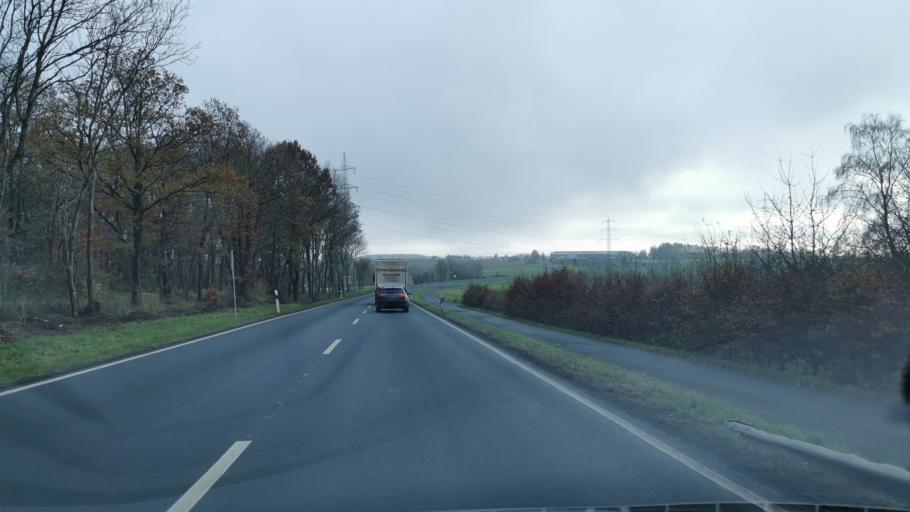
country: DE
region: Rheinland-Pfalz
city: Faid
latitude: 50.1565
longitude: 7.1109
